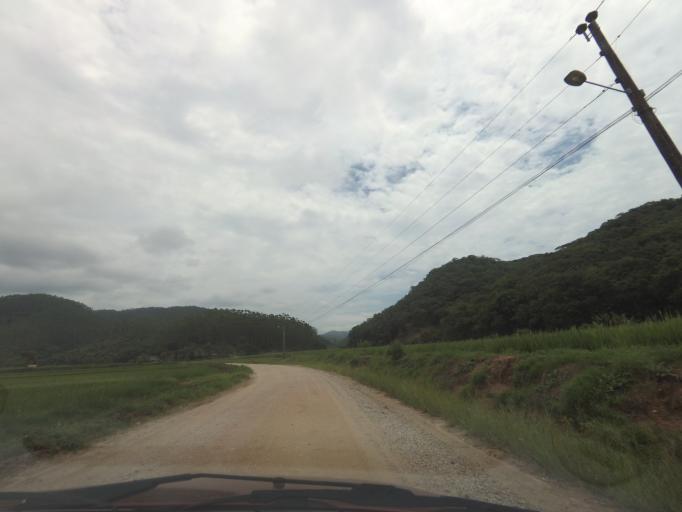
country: BR
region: Santa Catarina
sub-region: Gaspar
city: Gaspar
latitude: -26.9645
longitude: -49.0027
